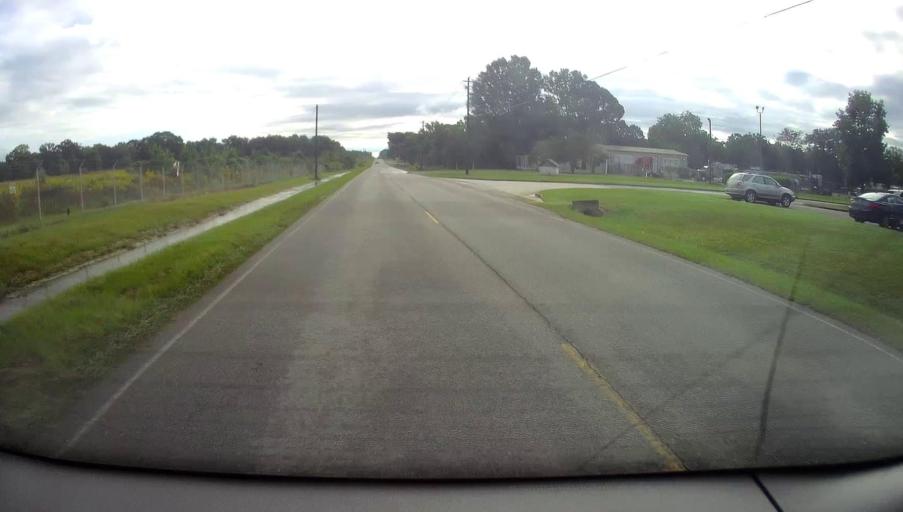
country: US
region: Georgia
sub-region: Peach County
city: Byron
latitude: 32.6519
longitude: -83.7393
